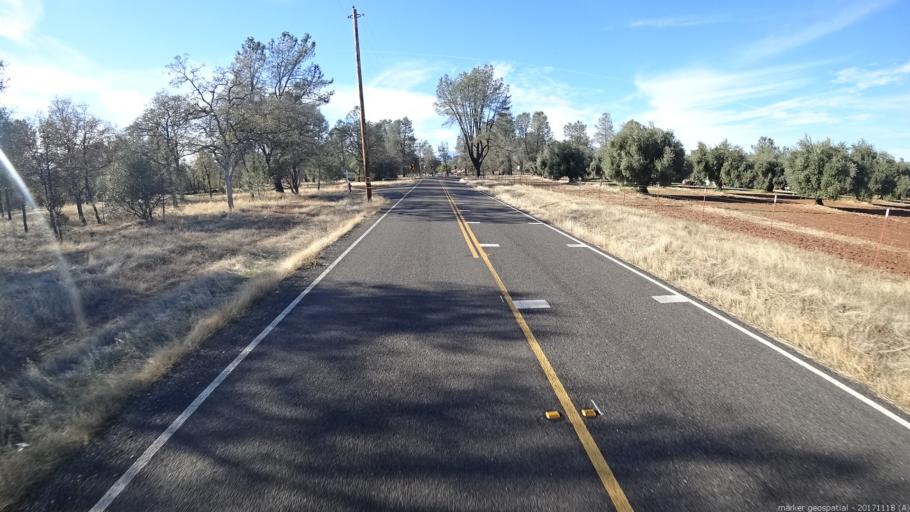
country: US
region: California
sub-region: Shasta County
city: Redding
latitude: 40.4508
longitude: -122.4536
